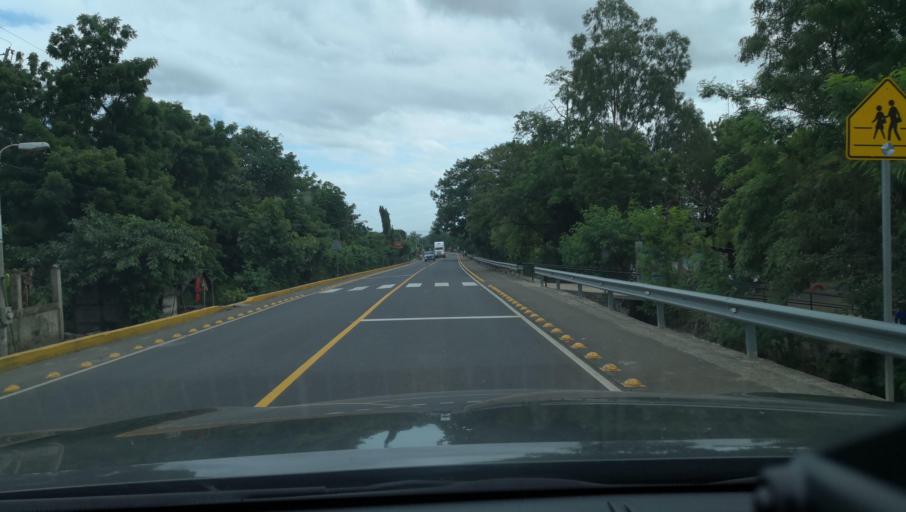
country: NI
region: Masaya
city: Nindiri
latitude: 12.0524
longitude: -86.1350
